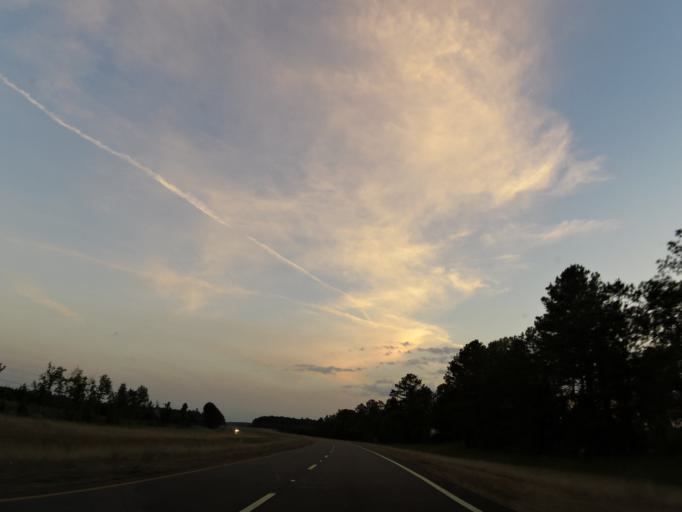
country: US
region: Mississippi
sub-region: Kemper County
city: De Kalb
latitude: 32.7222
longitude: -88.4774
